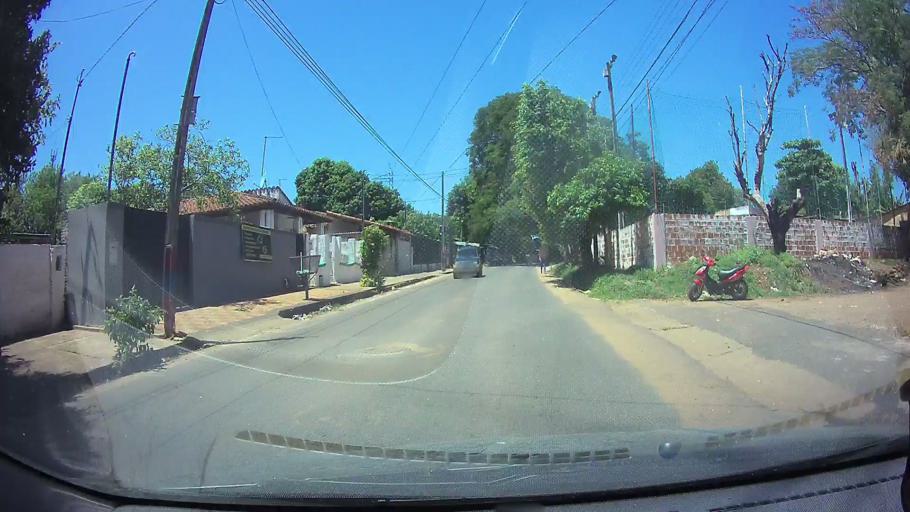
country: PY
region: Central
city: San Lorenzo
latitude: -25.3345
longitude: -57.4847
